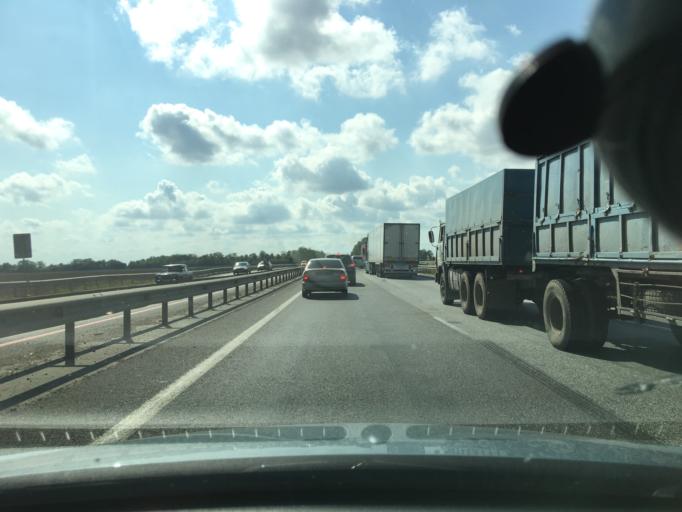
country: RU
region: Krasnodarskiy
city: Krasnoye
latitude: 46.6960
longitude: 39.6516
